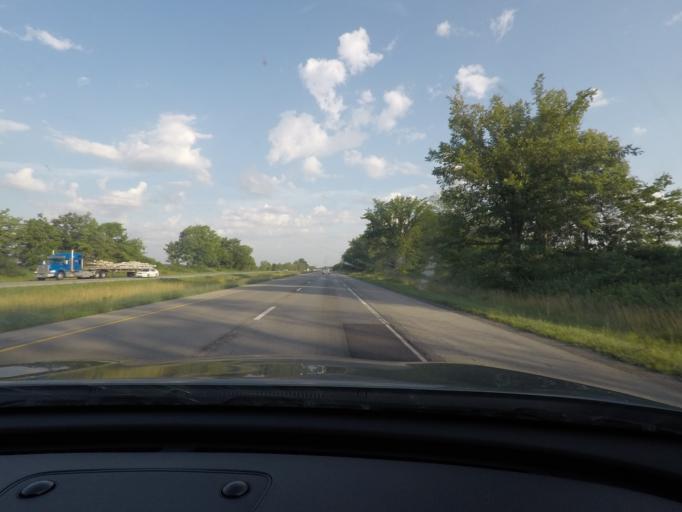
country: US
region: Illinois
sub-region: Jefferson County
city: Mount Vernon
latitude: 38.3482
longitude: -88.9815
